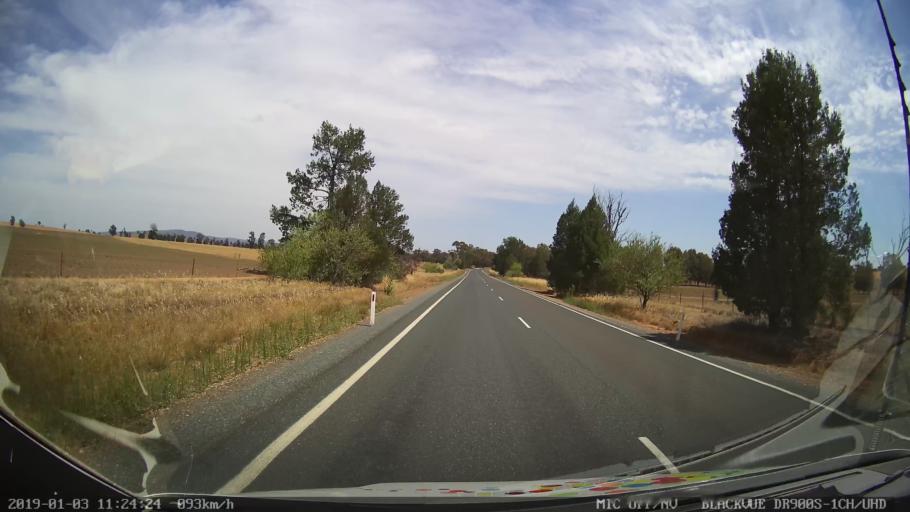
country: AU
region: New South Wales
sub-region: Weddin
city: Grenfell
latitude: -34.0518
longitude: 148.2352
